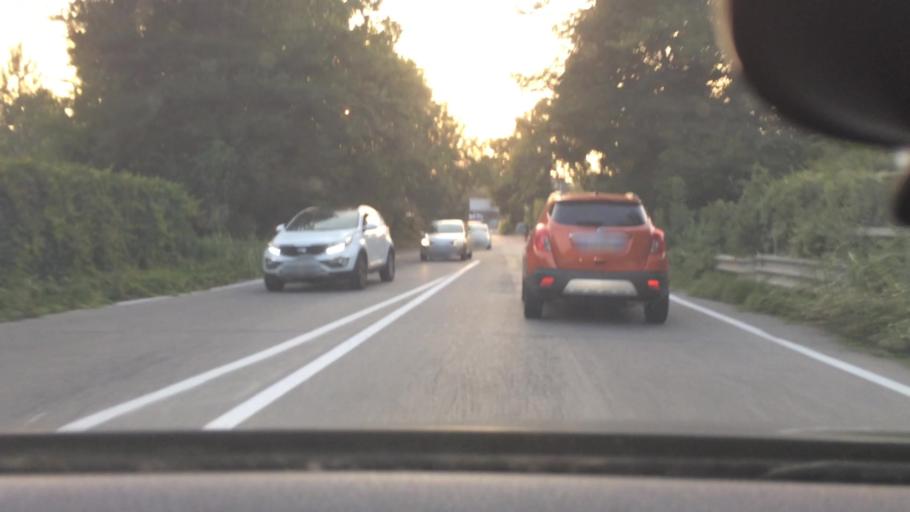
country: IT
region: Lombardy
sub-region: Provincia di Lecco
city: Tabiago-Cibrone
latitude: 45.7506
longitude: 9.2577
